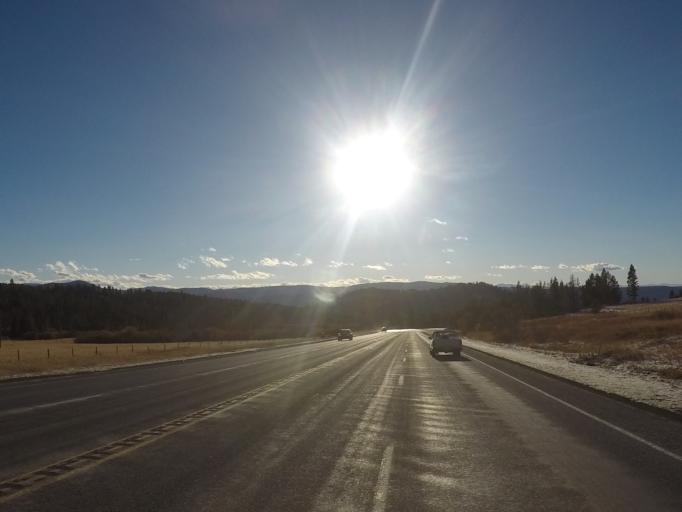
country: US
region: Montana
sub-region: Lewis and Clark County
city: Helena West Side
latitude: 46.5577
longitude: -112.3218
